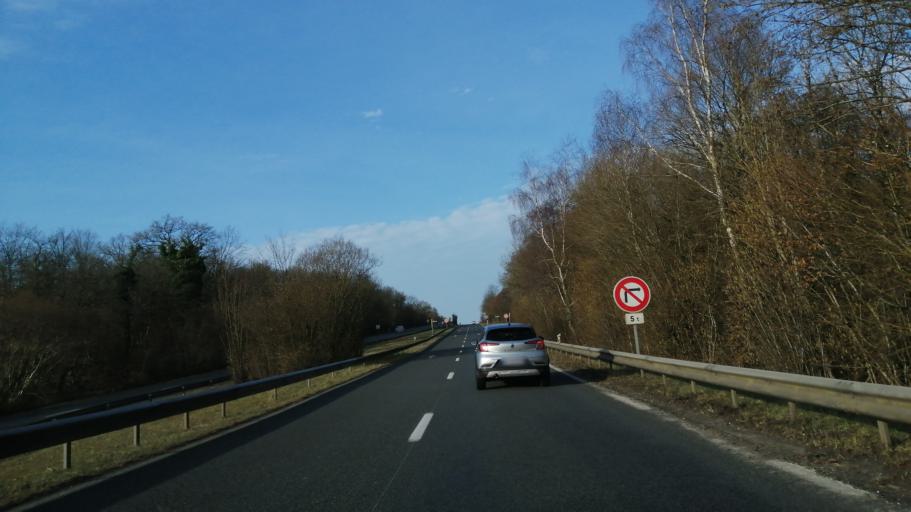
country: FR
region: Nord-Pas-de-Calais
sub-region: Departement du Pas-de-Calais
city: La Capelle-les-Boulogne
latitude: 50.7335
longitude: 1.7314
